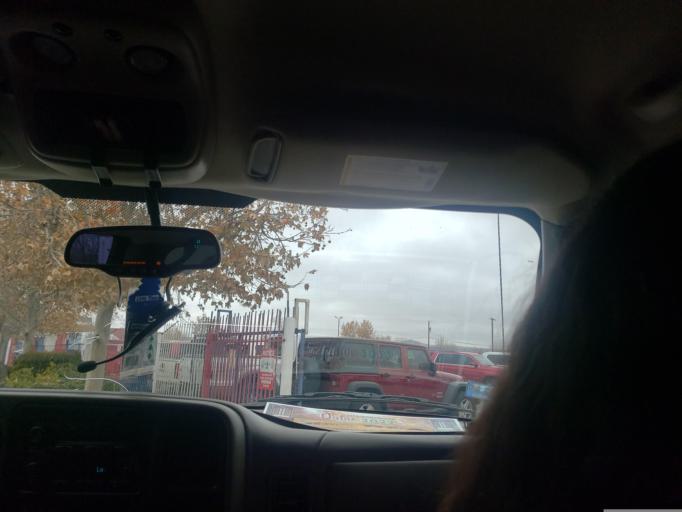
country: US
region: New Mexico
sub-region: Bernalillo County
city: Albuquerque
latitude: 35.0947
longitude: -106.7104
